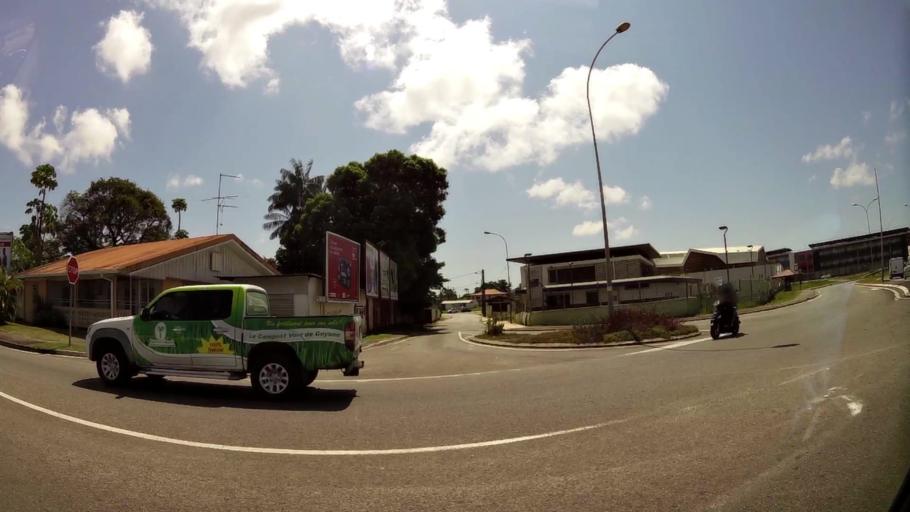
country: GF
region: Guyane
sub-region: Guyane
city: Cayenne
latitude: 4.9257
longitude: -52.3243
